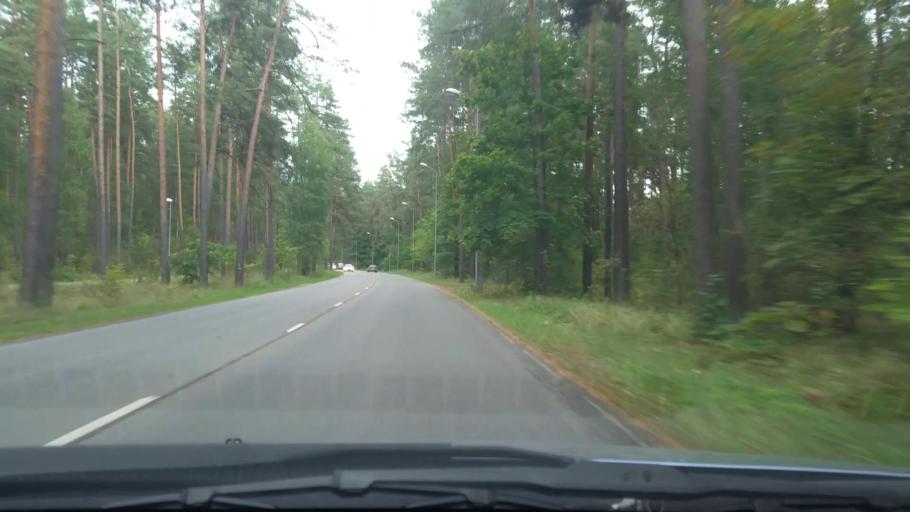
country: LV
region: Riga
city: Jaunciems
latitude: 56.9763
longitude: 24.2193
